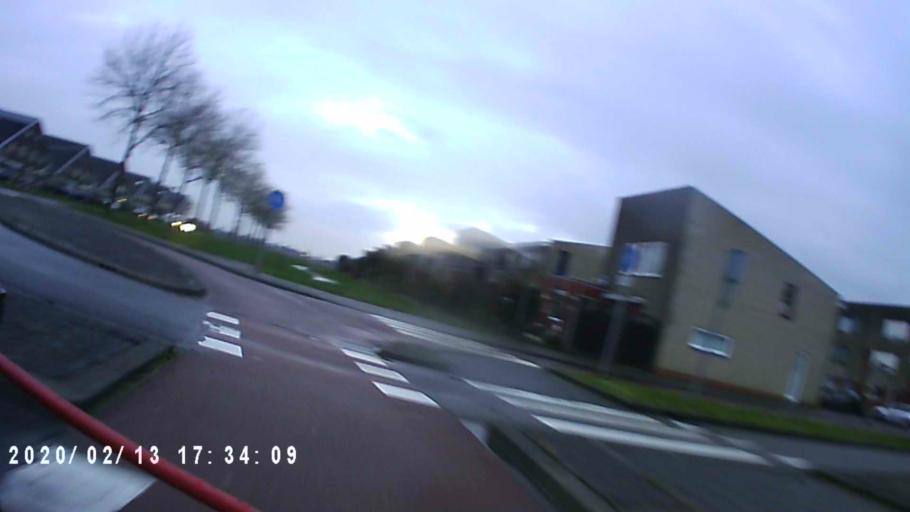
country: NL
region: Groningen
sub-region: Gemeente Groningen
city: Groningen
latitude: 53.2226
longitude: 6.5135
